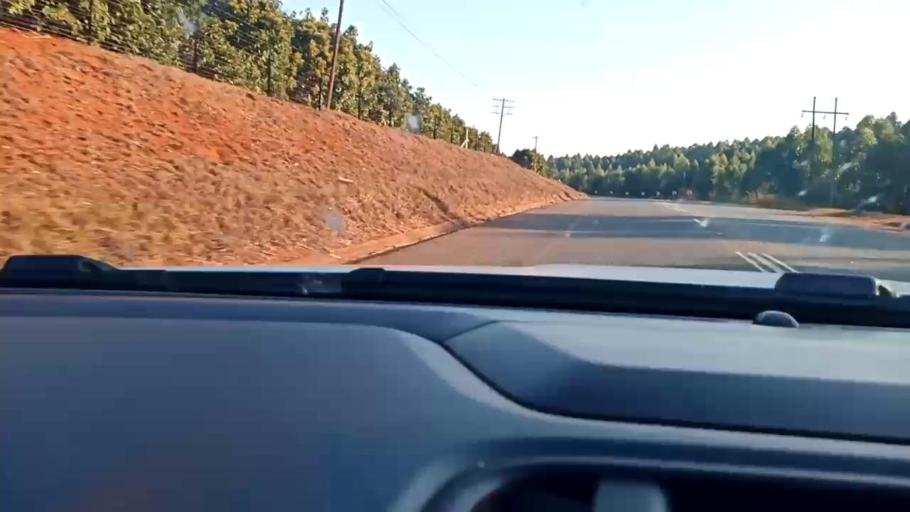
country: ZA
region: Limpopo
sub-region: Mopani District Municipality
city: Duiwelskloof
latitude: -23.7138
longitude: 30.1280
